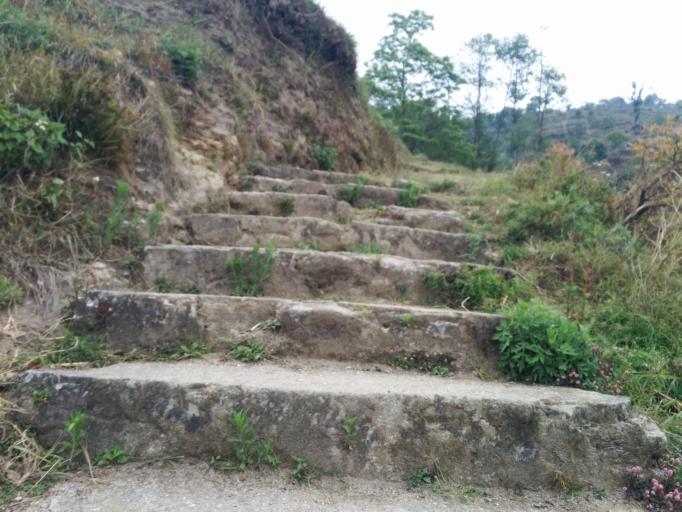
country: NP
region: Central Region
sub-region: Bagmati Zone
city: Bhaktapur
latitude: 27.7786
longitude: 85.4309
